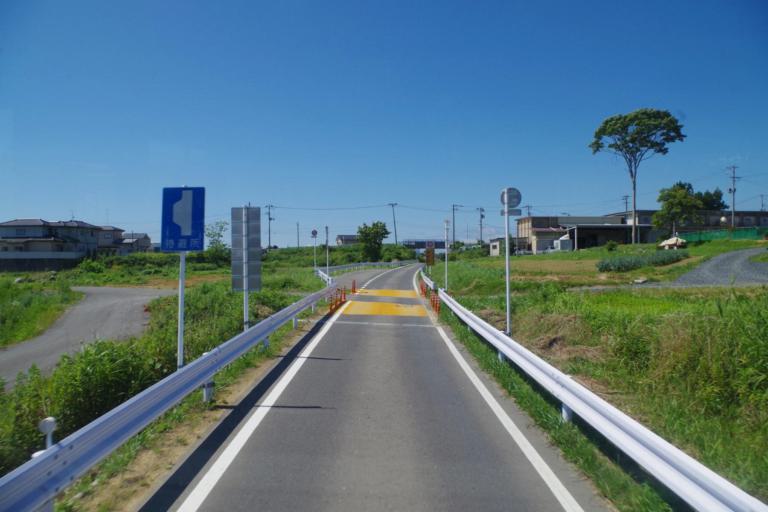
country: JP
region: Iwate
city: Ofunato
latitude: 38.8290
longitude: 141.5786
